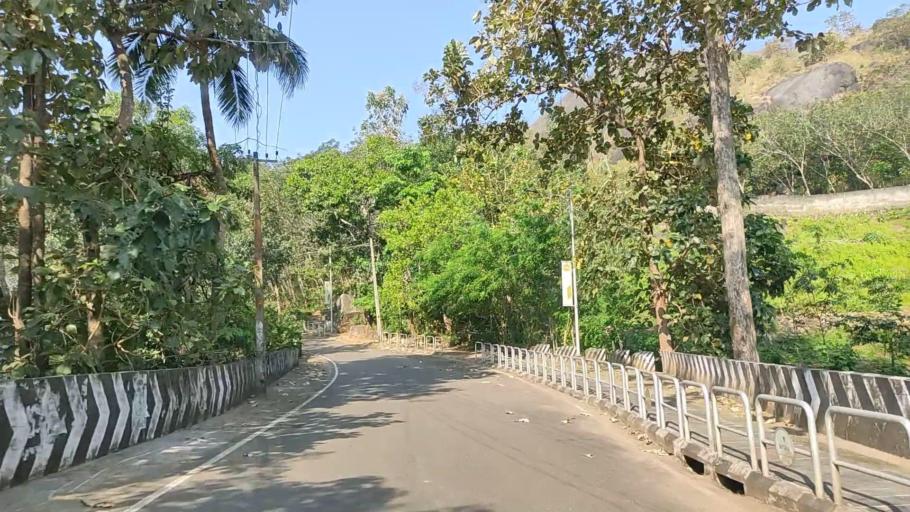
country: IN
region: Kerala
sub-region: Kollam
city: Punalur
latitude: 8.8609
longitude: 76.8686
